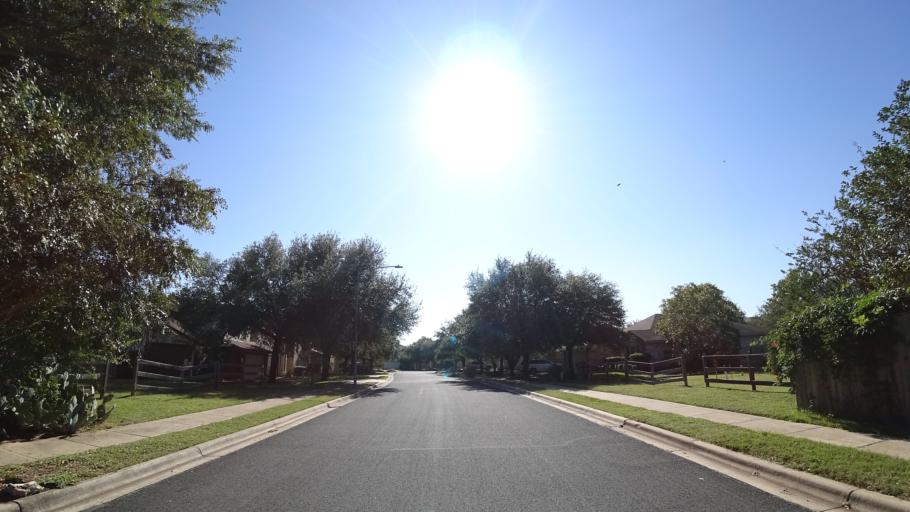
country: US
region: Texas
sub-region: Travis County
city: Shady Hollow
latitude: 30.1992
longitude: -97.8575
